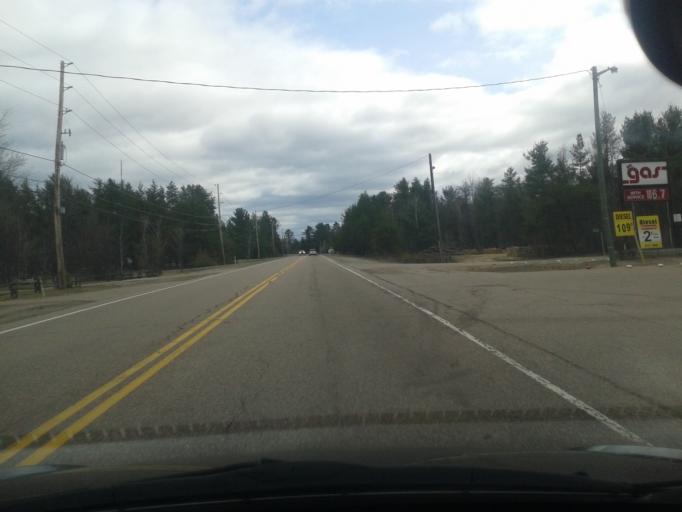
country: CA
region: Ontario
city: Deep River
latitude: 46.0564
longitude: -77.4747
